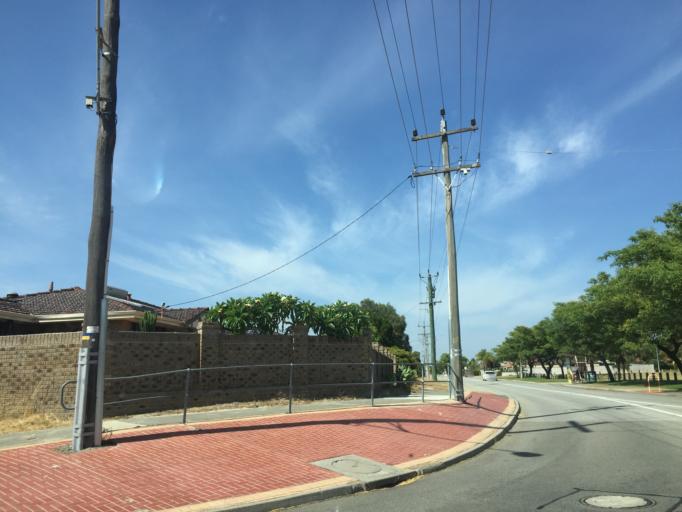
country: AU
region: Western Australia
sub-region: Gosnells
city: Thornlie
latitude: -32.0783
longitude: 115.9650
